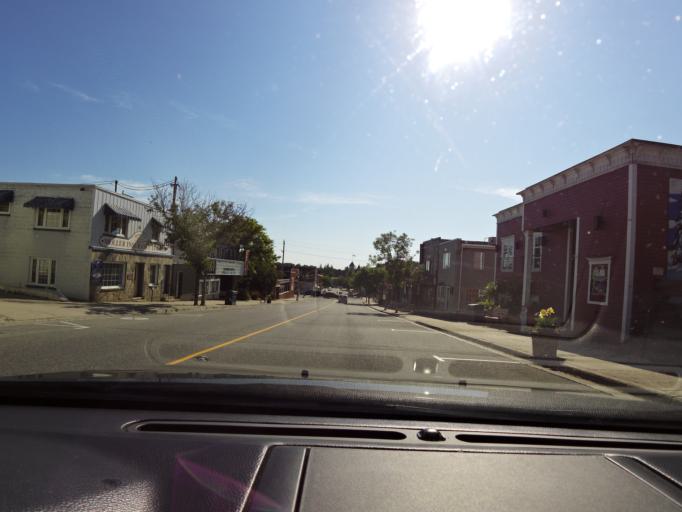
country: CA
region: Ontario
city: Huntsville
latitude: 45.3259
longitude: -79.2215
